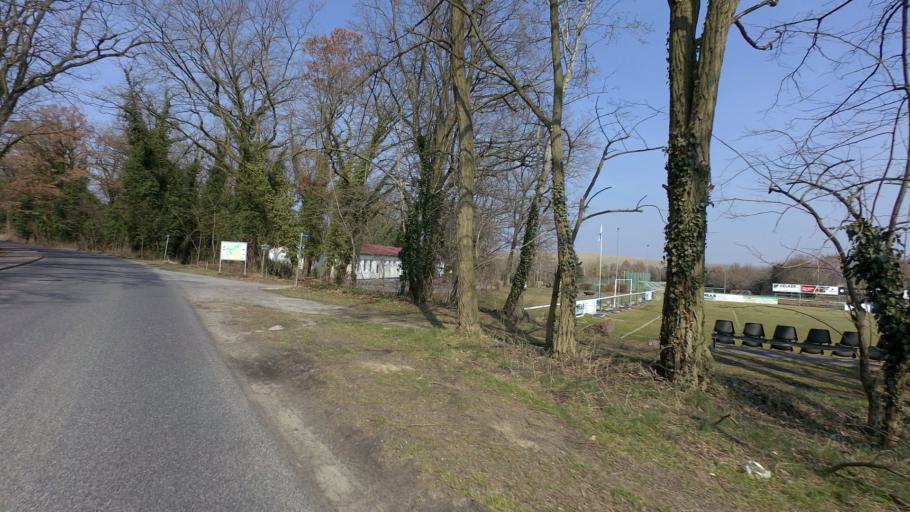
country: DE
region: Brandenburg
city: Gross Kreutz
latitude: 52.4435
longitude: 12.7823
